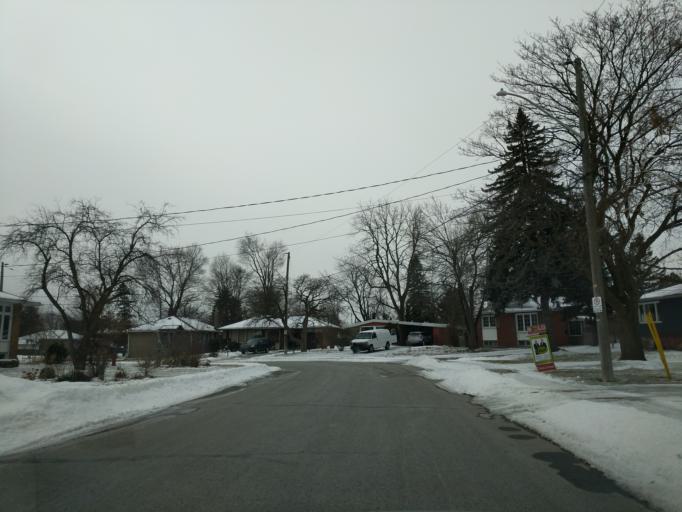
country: CA
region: Ontario
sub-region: York
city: Richmond Hill
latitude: 43.8775
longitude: -79.4193
